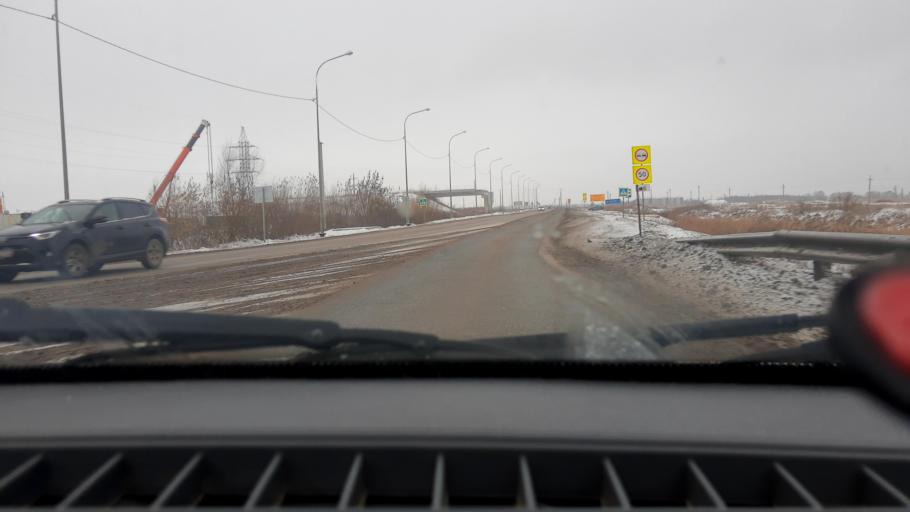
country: RU
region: Bashkortostan
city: Asanovo
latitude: 54.9000
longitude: 55.6322
